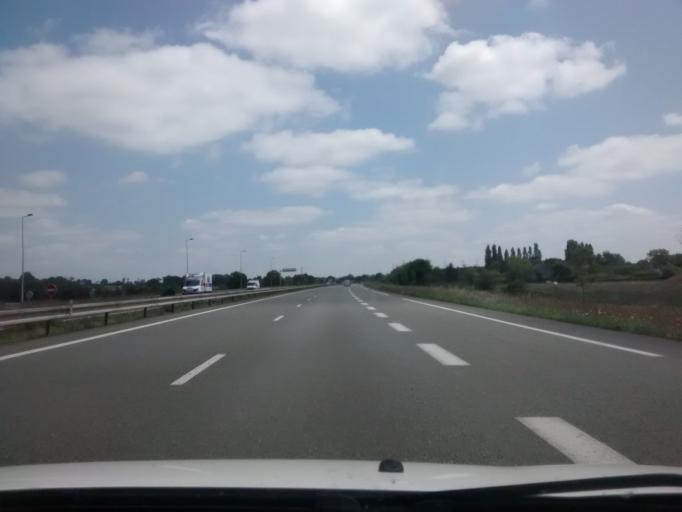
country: FR
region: Pays de la Loire
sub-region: Departement de la Mayenne
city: Bonchamp-les-Laval
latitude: 48.0959
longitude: -0.6938
